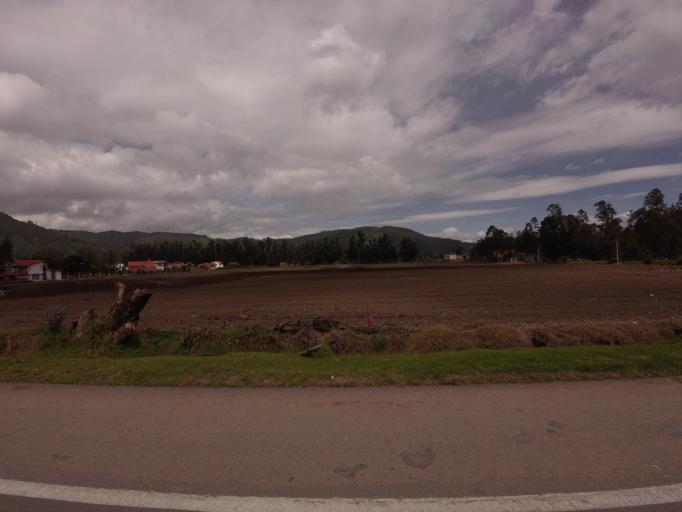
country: CO
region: Boyaca
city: Tibasosa
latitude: 5.7772
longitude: -72.9963
